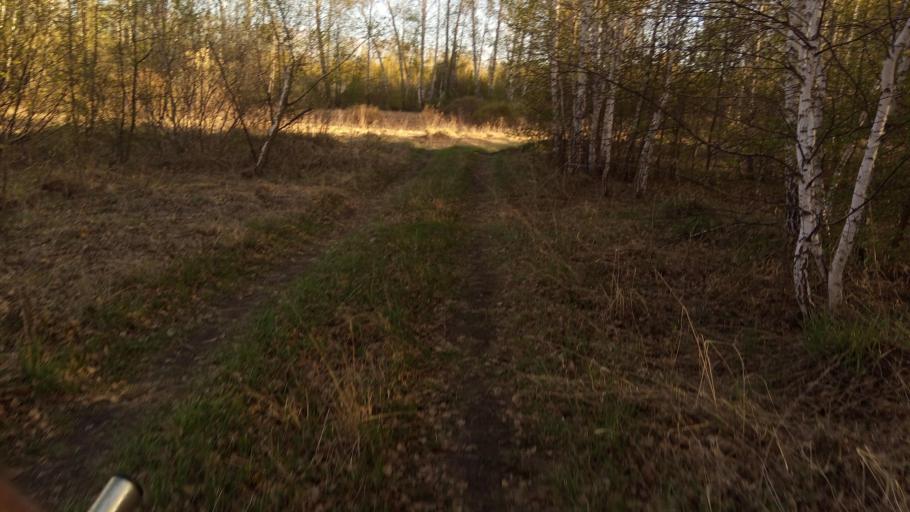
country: RU
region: Chelyabinsk
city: Timiryazevskiy
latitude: 54.9923
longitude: 60.8591
